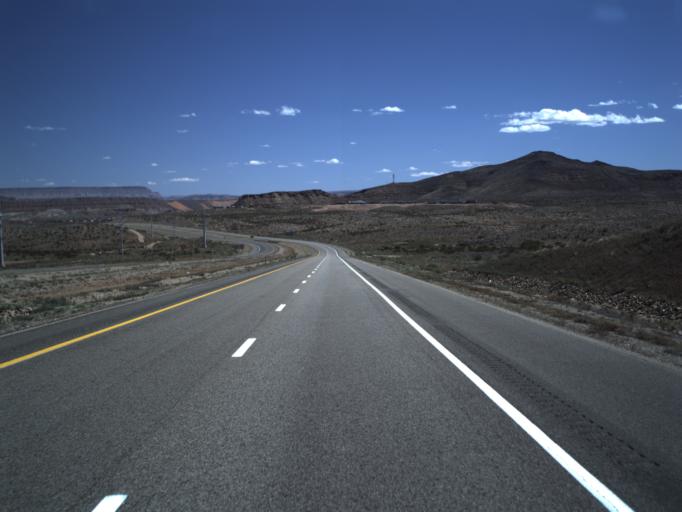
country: US
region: Utah
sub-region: Washington County
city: Saint George
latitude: 37.0050
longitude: -113.5351
